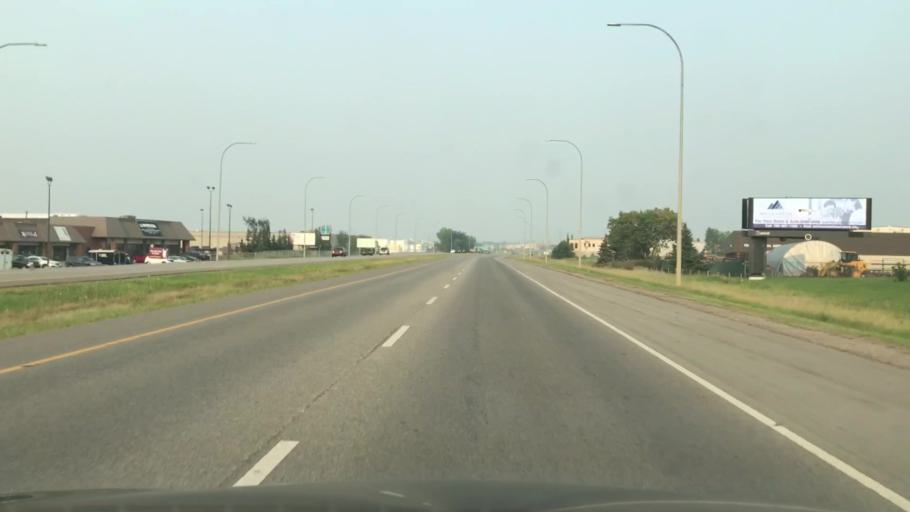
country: CA
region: Alberta
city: Edmonton
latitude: 53.5158
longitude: -113.4083
